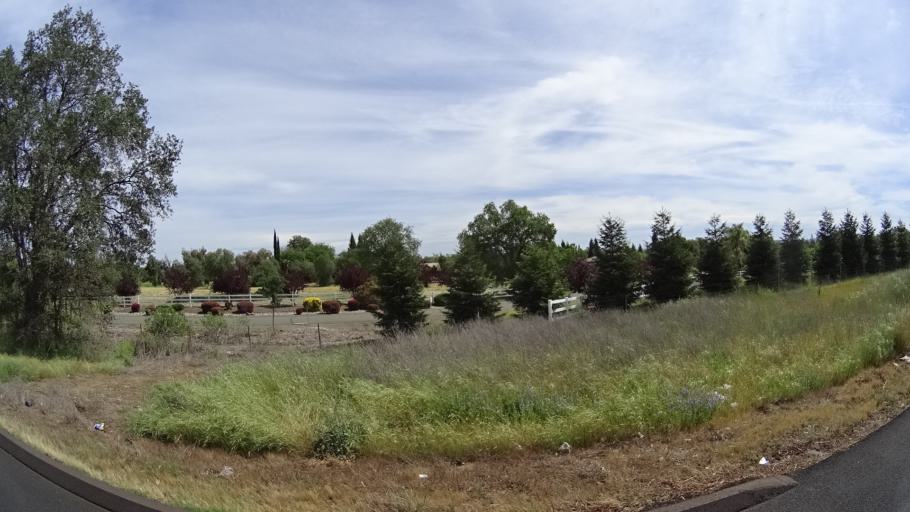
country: US
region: California
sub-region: Placer County
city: Loomis
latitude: 38.8336
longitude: -121.2183
